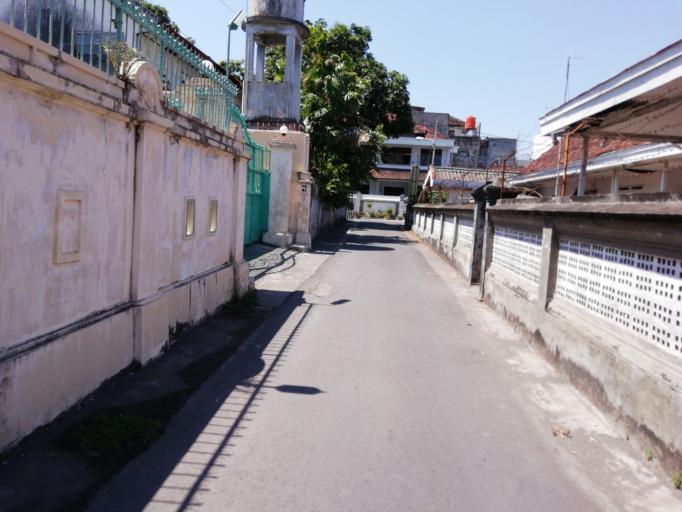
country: ID
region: Bali
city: Denpasar
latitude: -8.6732
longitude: 115.2144
